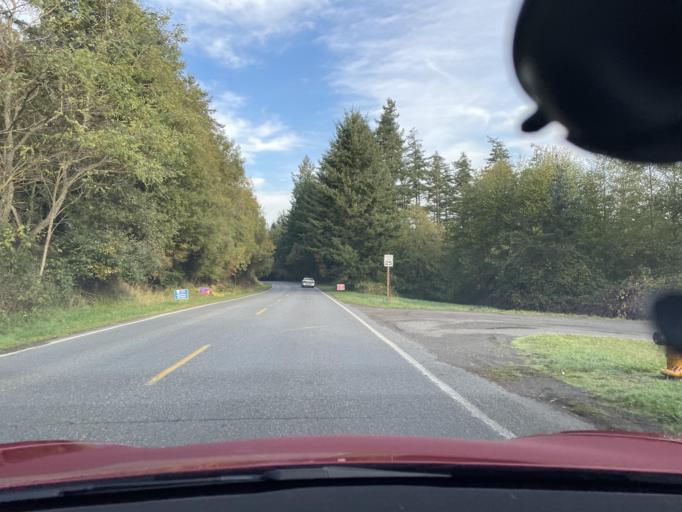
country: US
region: Washington
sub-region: San Juan County
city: Friday Harbor
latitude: 48.5372
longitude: -123.0319
